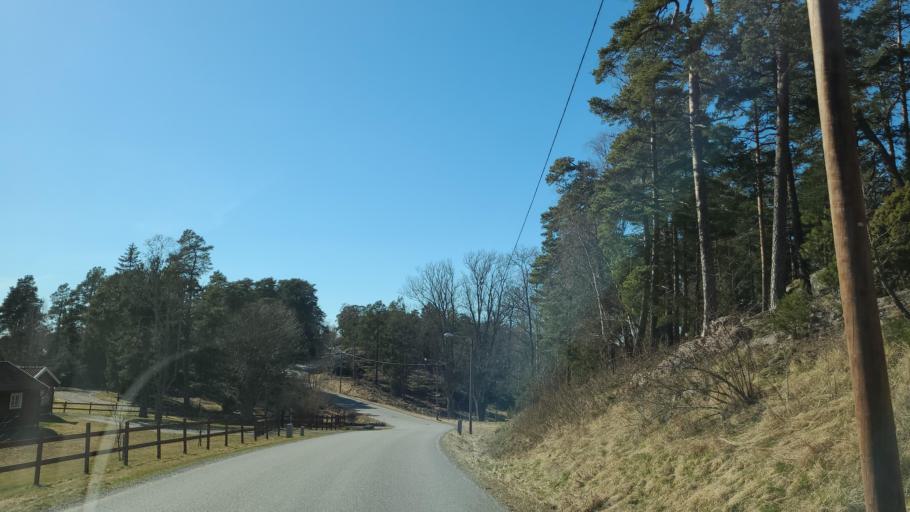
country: SE
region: Stockholm
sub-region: Varmdo Kommun
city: Hemmesta
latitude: 59.2780
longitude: 18.5648
